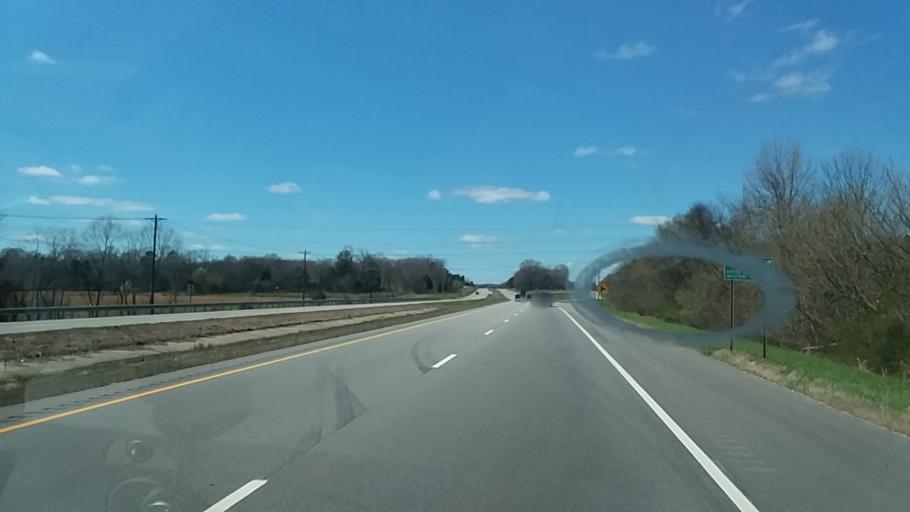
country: US
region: Alabama
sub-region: Colbert County
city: Cherokee
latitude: 34.7301
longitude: -87.8495
